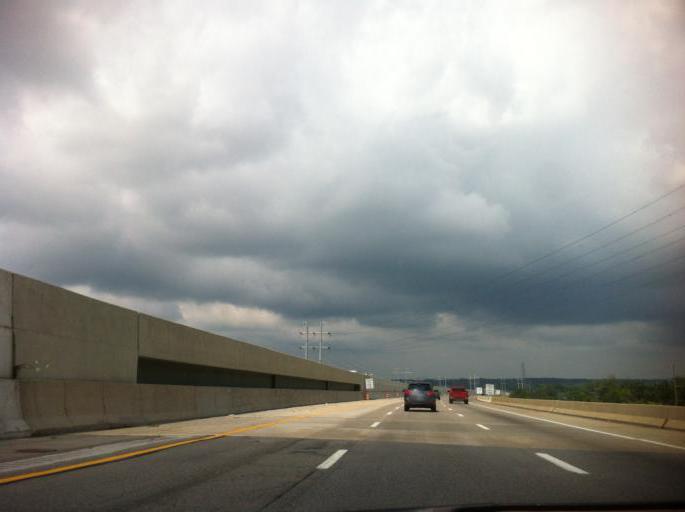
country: US
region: Ohio
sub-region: Cuyahoga County
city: North Royalton
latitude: 41.3053
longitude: -81.7438
